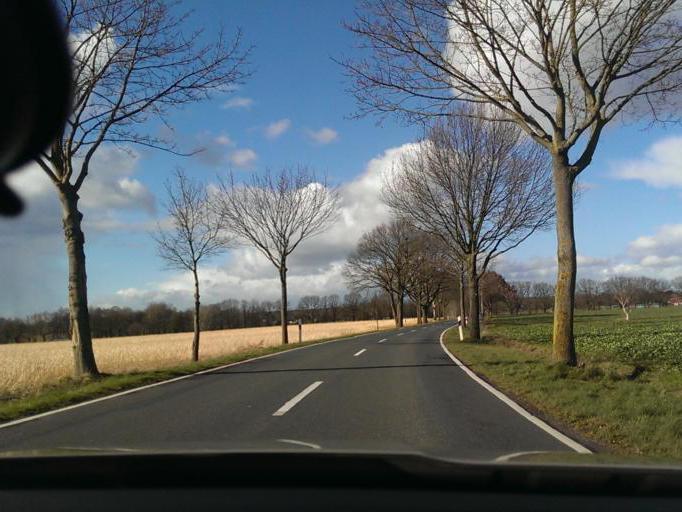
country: DE
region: Lower Saxony
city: Elze
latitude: 52.5407
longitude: 9.6838
